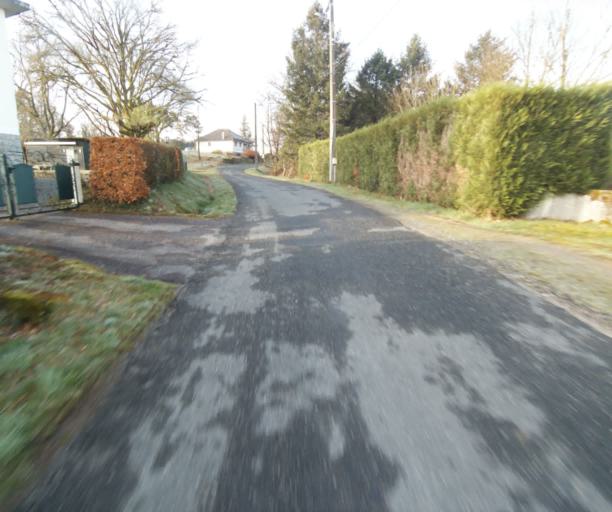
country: FR
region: Limousin
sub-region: Departement de la Correze
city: Correze
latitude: 45.3262
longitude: 1.8664
